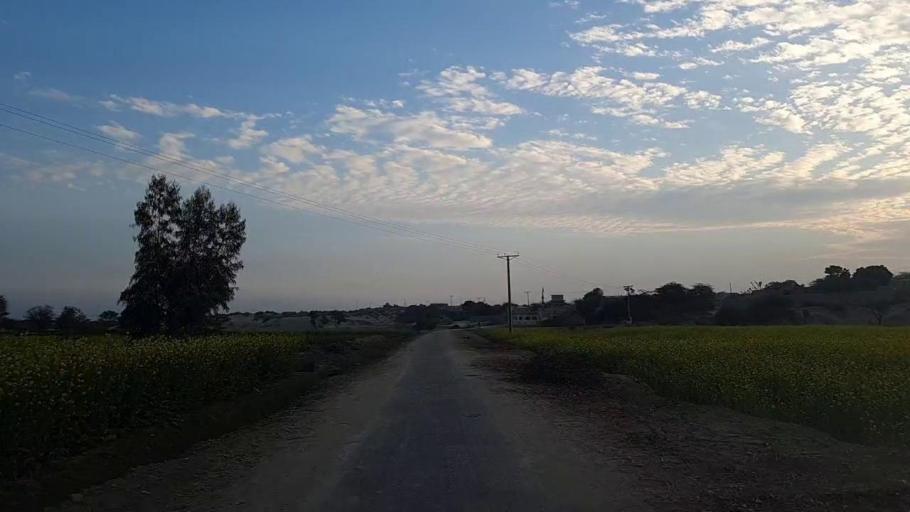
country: PK
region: Sindh
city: Daur
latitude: 26.4141
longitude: 68.4678
